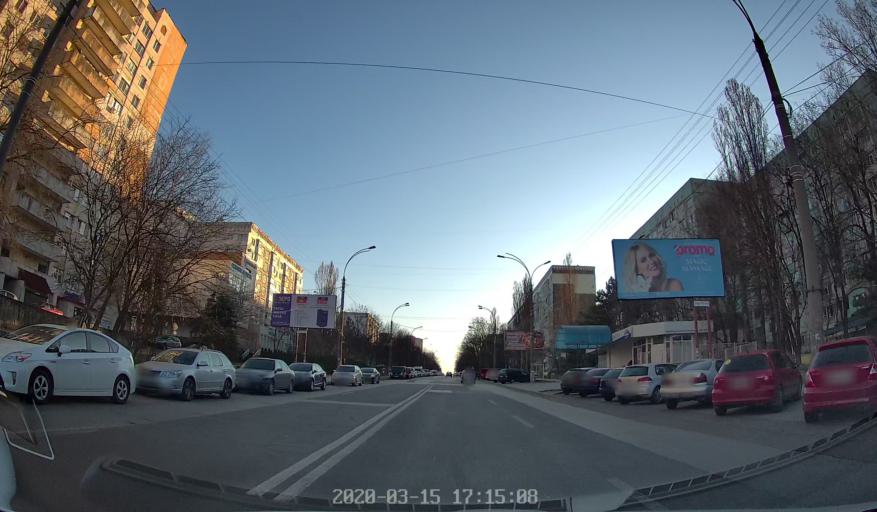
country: MD
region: Chisinau
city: Chisinau
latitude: 46.9703
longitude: 28.8466
